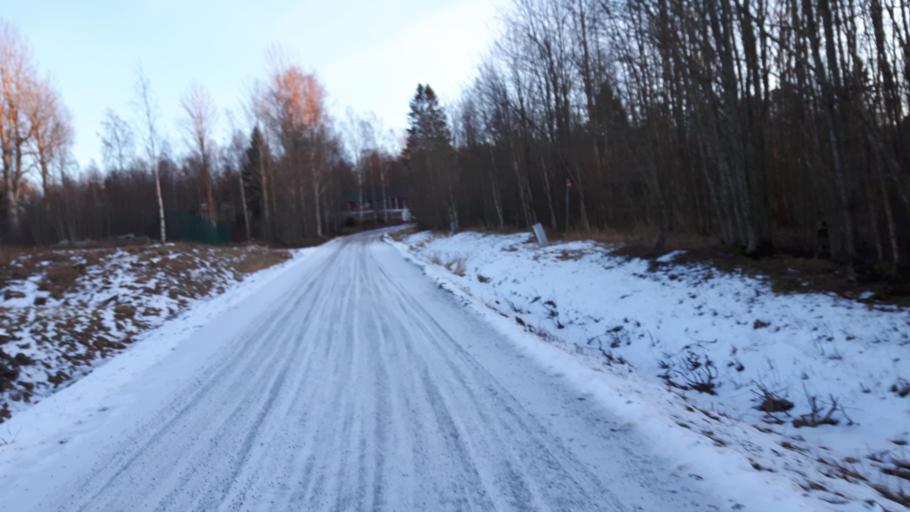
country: SE
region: Vaesternorrland
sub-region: Haernoesands Kommun
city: Haernoesand
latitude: 62.6203
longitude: 17.9362
